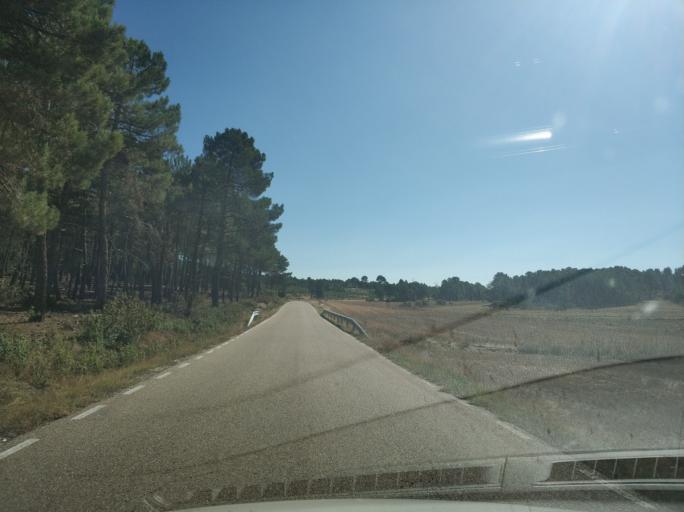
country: ES
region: Castille and Leon
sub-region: Provincia de Soria
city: Espeja de San Marcelino
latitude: 41.7789
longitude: -3.1860
